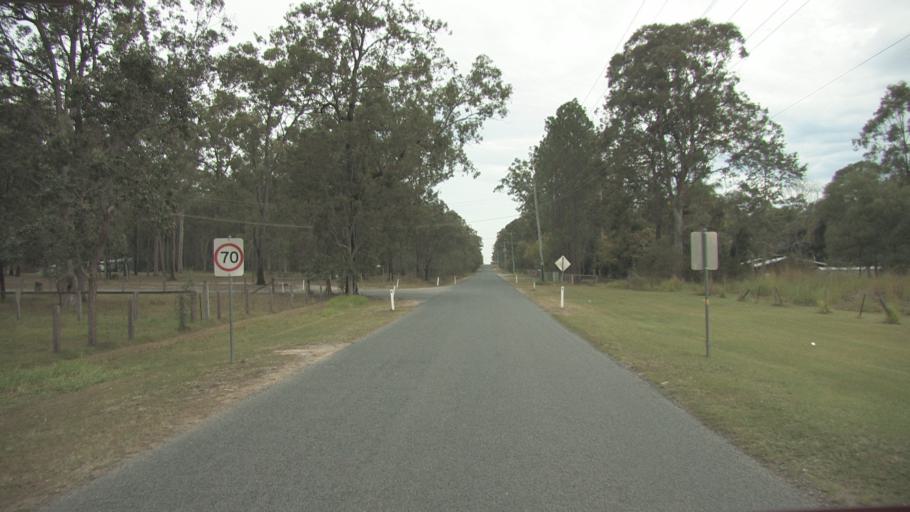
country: AU
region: Queensland
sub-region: Logan
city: Chambers Flat
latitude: -27.7911
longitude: 153.1209
